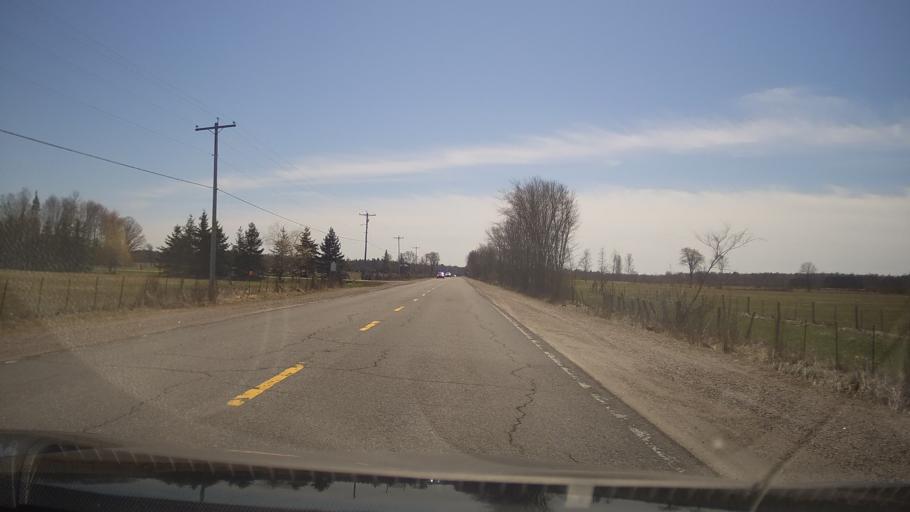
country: CA
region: Ontario
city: Arnprior
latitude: 45.5454
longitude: -76.3449
